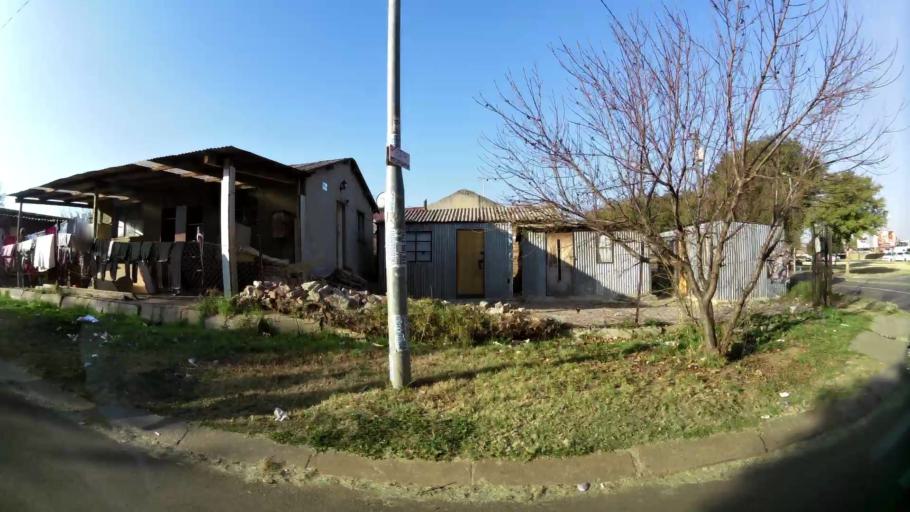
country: ZA
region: Gauteng
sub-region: City of Johannesburg Metropolitan Municipality
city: Soweto
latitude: -26.2631
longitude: 27.8806
